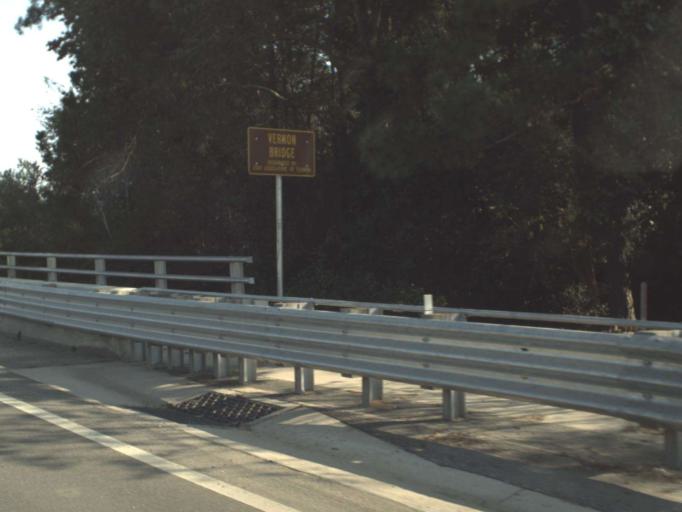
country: US
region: Florida
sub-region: Holmes County
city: Bonifay
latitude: 30.6262
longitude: -85.7122
